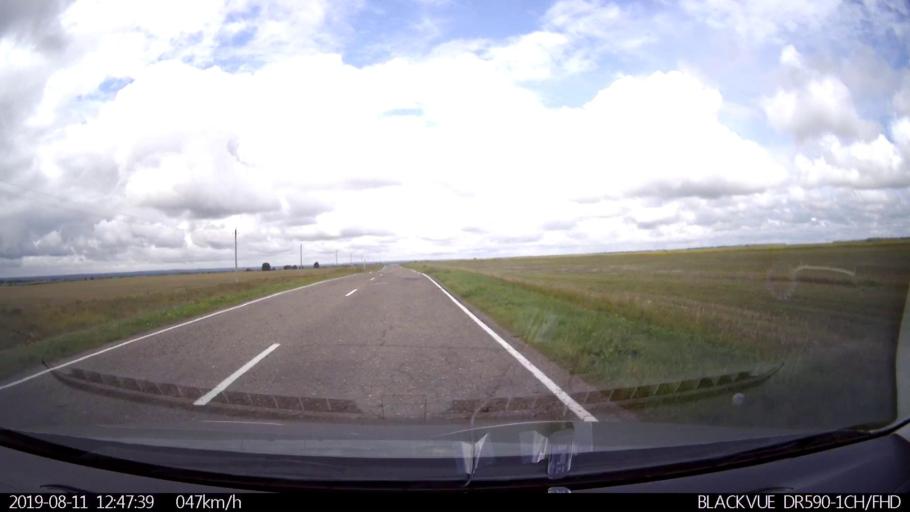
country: RU
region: Ulyanovsk
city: Ignatovka
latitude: 53.8703
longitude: 47.7068
